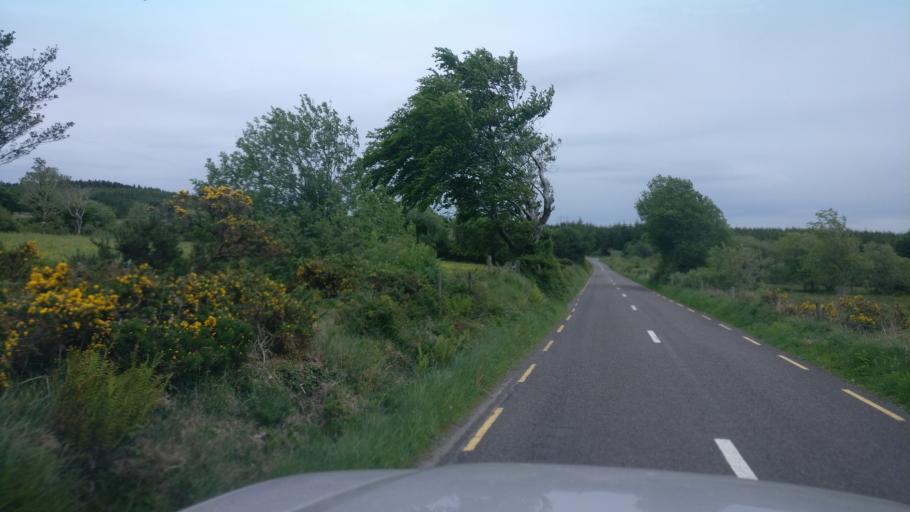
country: IE
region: Connaught
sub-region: County Galway
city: Loughrea
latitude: 53.0723
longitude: -8.5841
